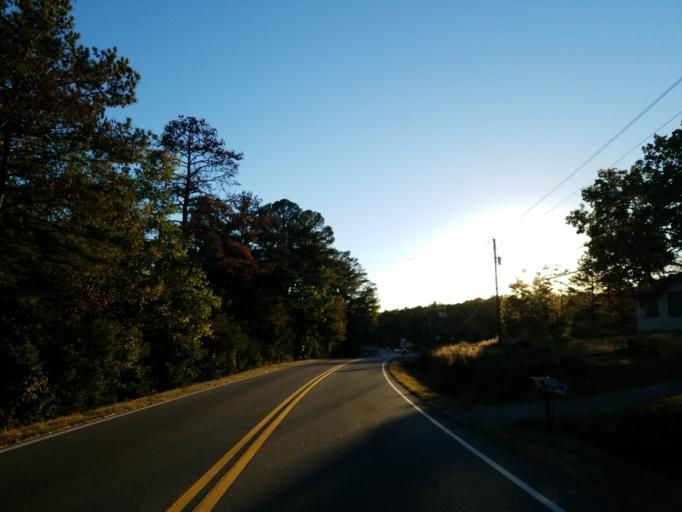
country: US
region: Georgia
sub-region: Forsyth County
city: Cumming
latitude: 34.2510
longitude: -84.1094
